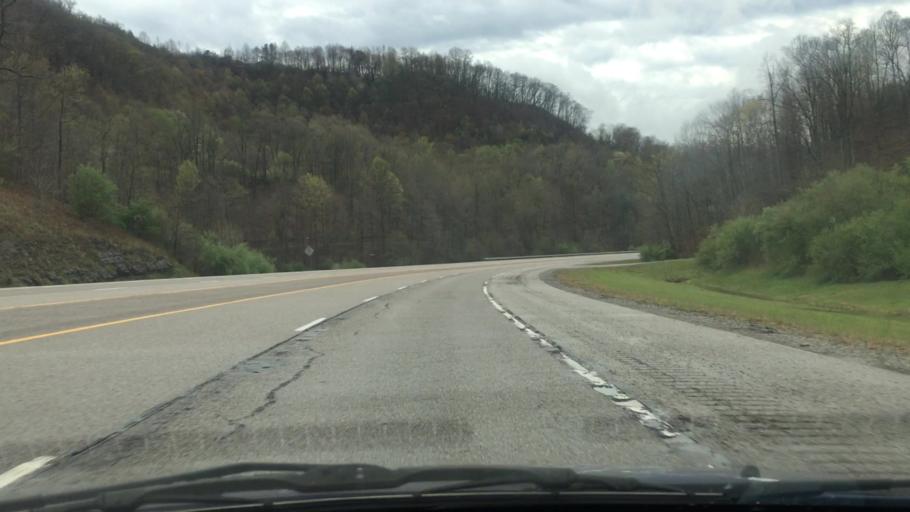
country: US
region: Kentucky
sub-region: Letcher County
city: Jenkins
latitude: 37.2121
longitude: -82.6240
